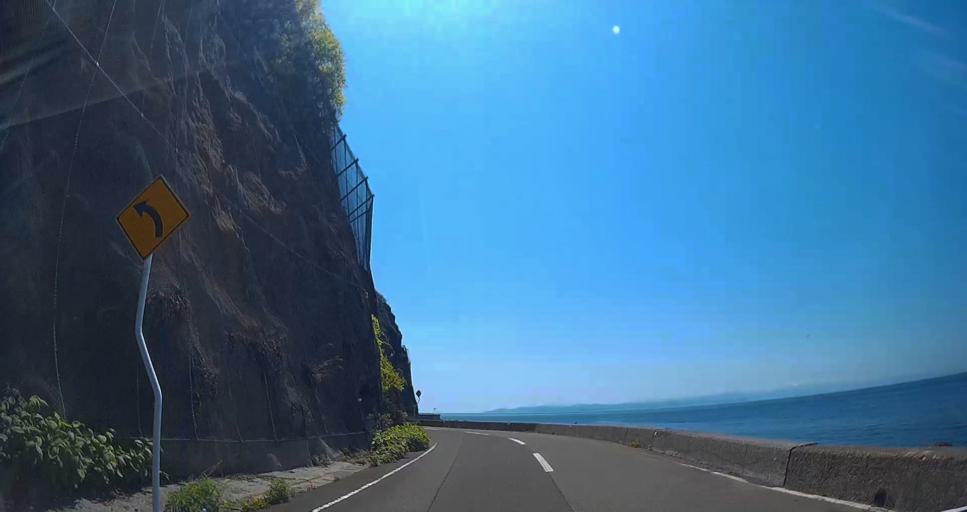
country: JP
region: Aomori
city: Aomori Shi
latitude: 41.1333
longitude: 140.7805
